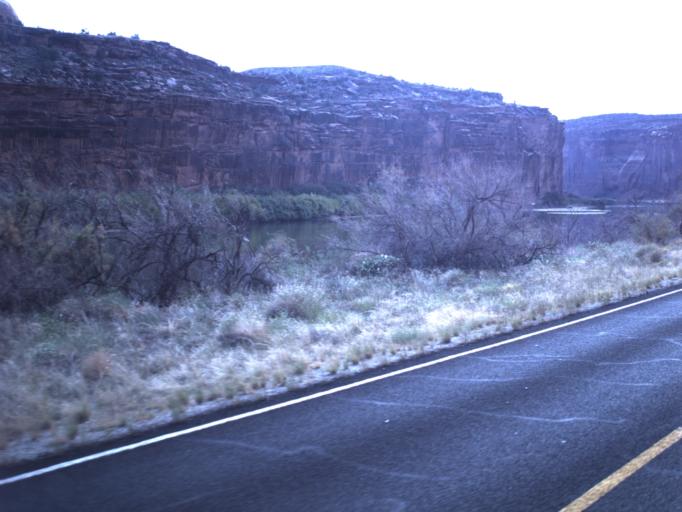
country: US
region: Utah
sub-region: Grand County
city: Moab
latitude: 38.5781
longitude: -109.6469
